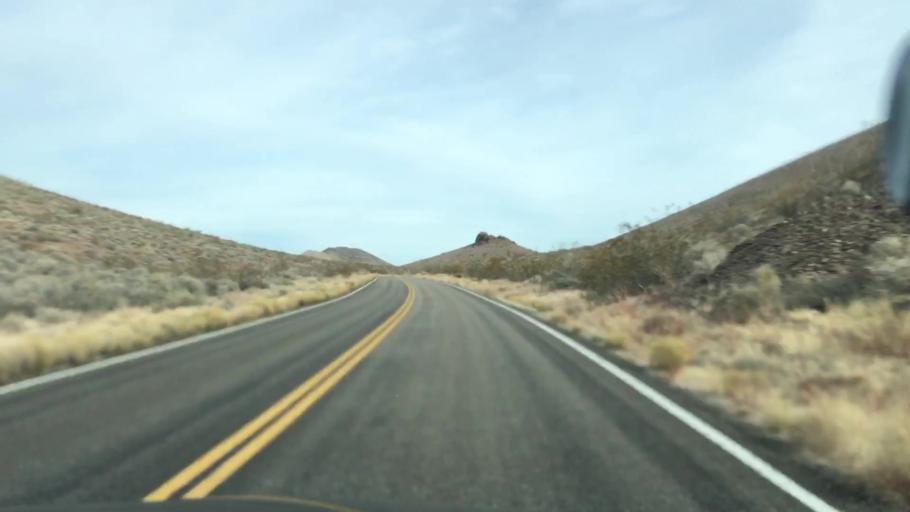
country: US
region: Nevada
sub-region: Nye County
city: Beatty
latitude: 36.7800
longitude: -116.9321
